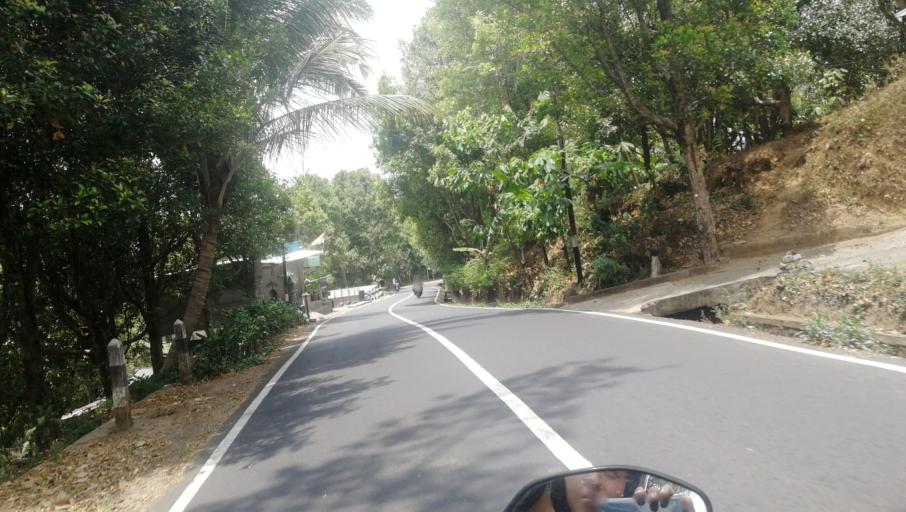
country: ID
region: Bali
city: Munduk
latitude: -8.2645
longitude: 115.0480
